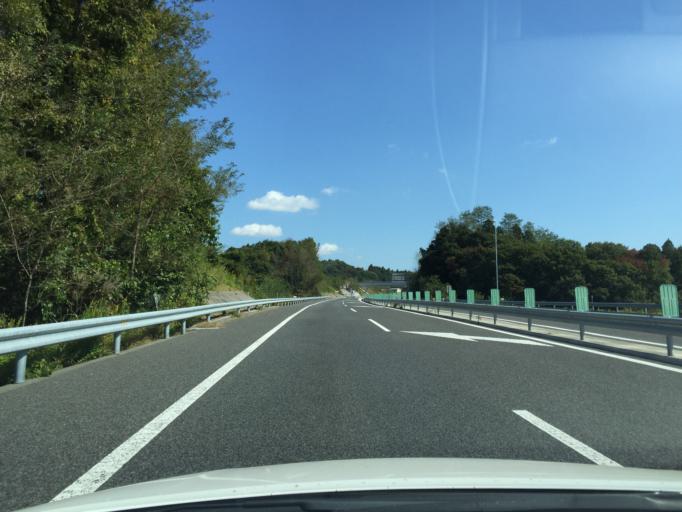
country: JP
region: Fukushima
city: Ishikawa
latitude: 37.2033
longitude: 140.4442
